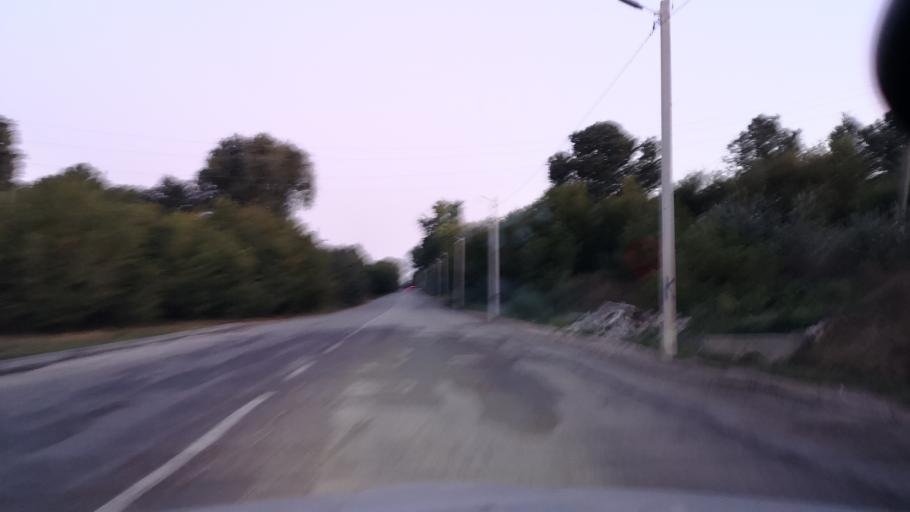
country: MD
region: Orhei
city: Orhei
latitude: 47.4020
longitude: 28.8186
